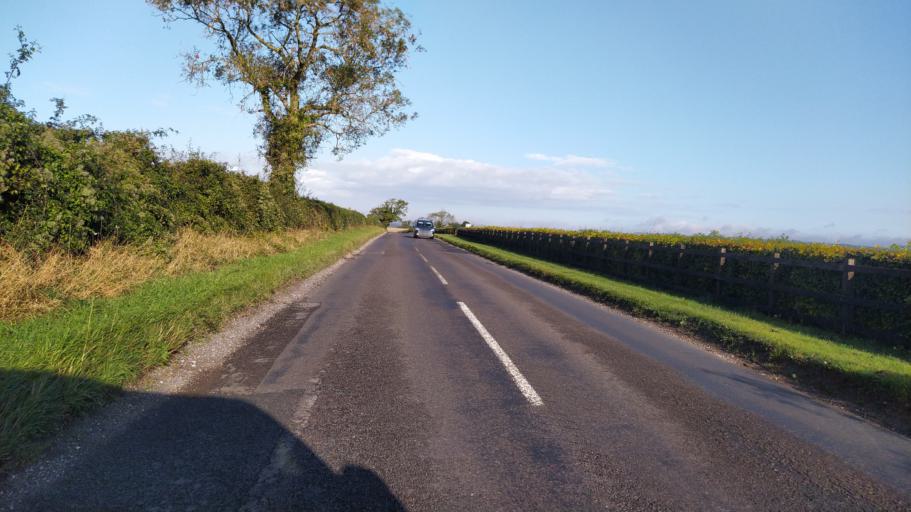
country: GB
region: England
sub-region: Wiltshire
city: Bower Chalke
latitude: 50.9038
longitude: -2.0321
